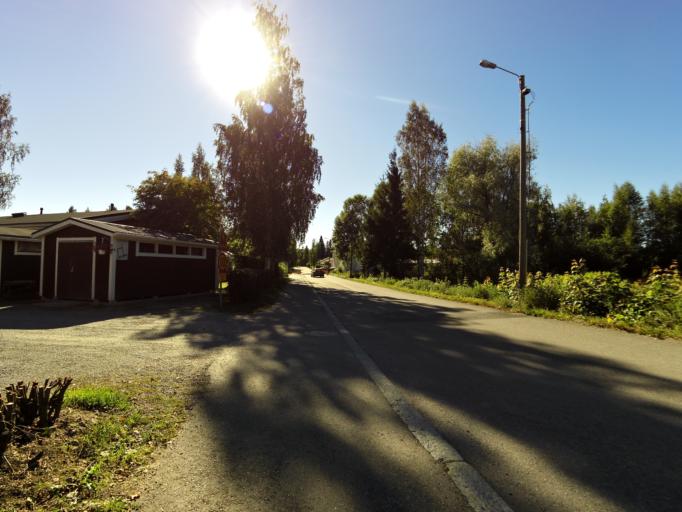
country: FI
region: Pirkanmaa
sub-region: Tampere
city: Yloejaervi
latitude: 61.5103
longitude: 23.6034
